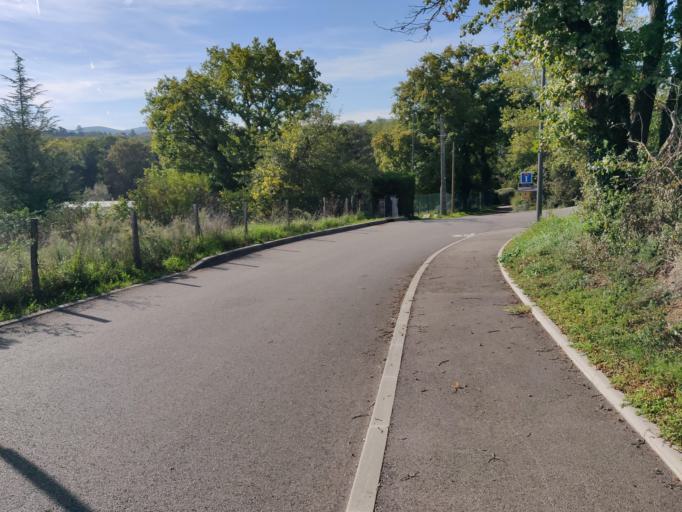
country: FR
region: Rhone-Alpes
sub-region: Departement du Rhone
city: Craponne
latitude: 45.7370
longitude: 4.7125
